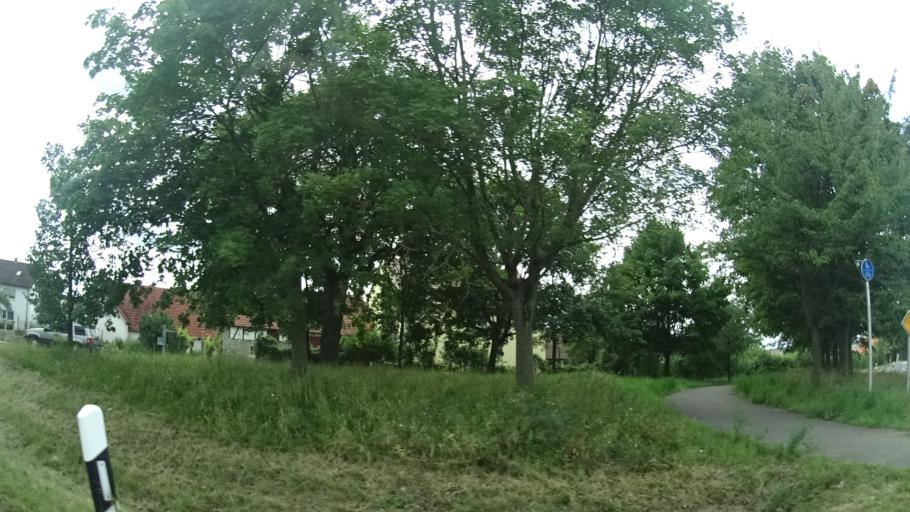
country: DE
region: Bavaria
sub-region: Regierungsbezirk Unterfranken
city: Donnersdorf
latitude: 49.9845
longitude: 10.3851
